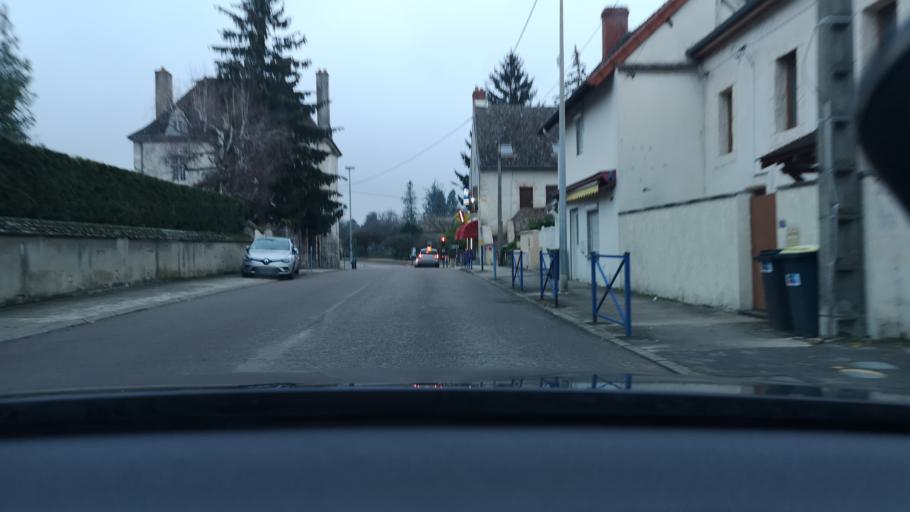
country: FR
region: Bourgogne
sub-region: Departement de Saone-et-Loire
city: Saint-Remy
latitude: 46.7626
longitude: 4.8401
